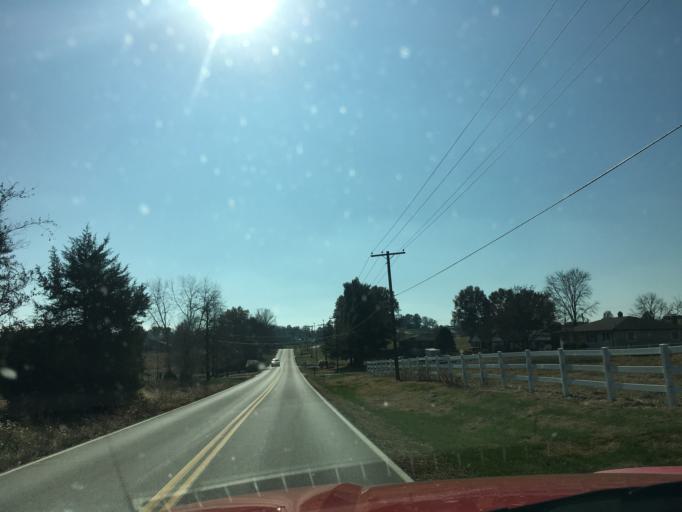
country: US
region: Missouri
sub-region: Cole County
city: Wardsville
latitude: 38.5032
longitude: -92.1760
